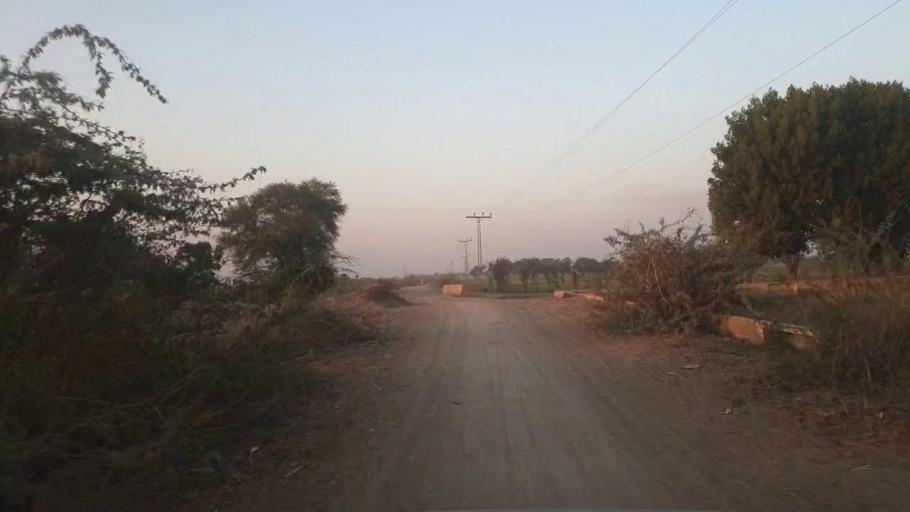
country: PK
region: Sindh
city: Chambar
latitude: 25.2990
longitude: 68.9076
